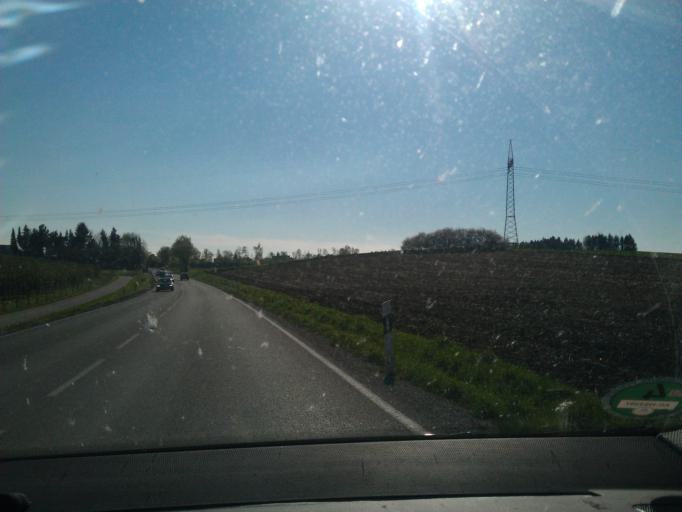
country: DE
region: Bavaria
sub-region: Swabia
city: Friedberg
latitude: 48.3702
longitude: 11.0019
